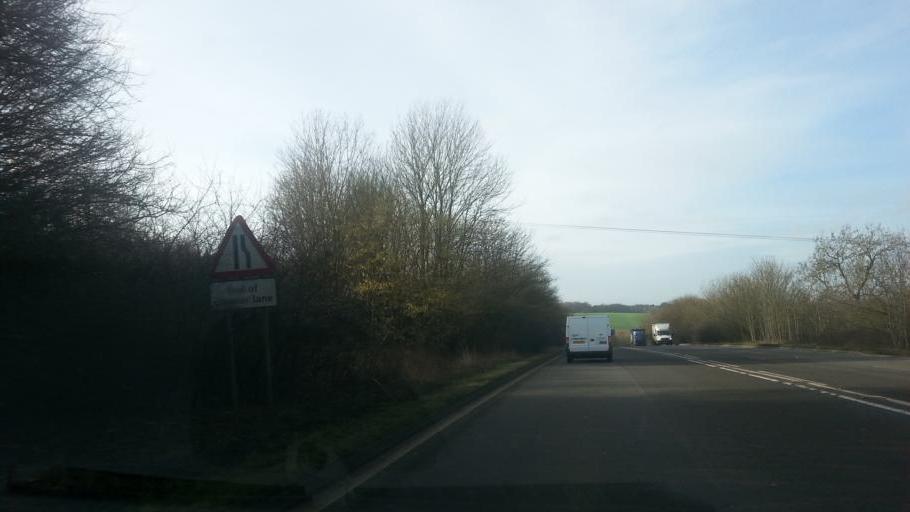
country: GB
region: England
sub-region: District of Rutland
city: Ridlington
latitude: 52.5940
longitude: -0.8399
